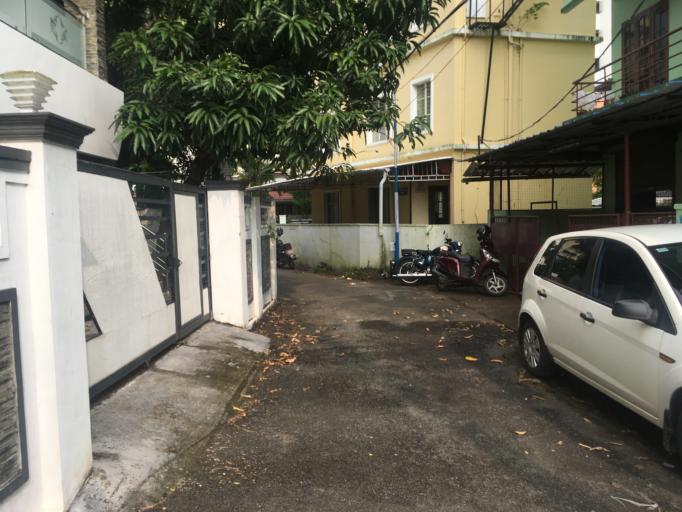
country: IN
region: Kerala
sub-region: Ernakulam
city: Cochin
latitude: 9.9887
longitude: 76.2779
